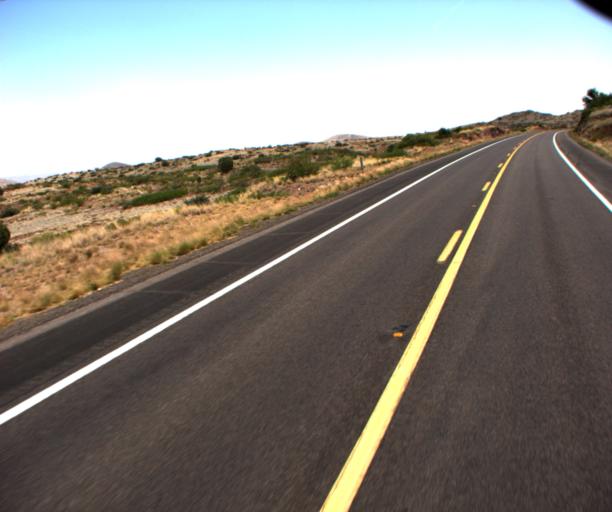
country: US
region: Arizona
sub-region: Greenlee County
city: Clifton
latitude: 32.7616
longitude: -109.2473
